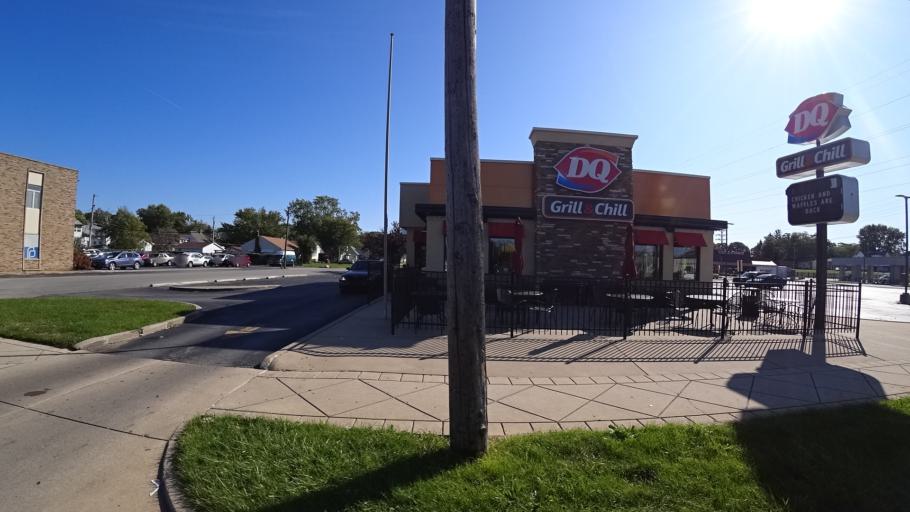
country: US
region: Indiana
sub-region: LaPorte County
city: Michigan City
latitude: 41.7014
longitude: -86.8941
